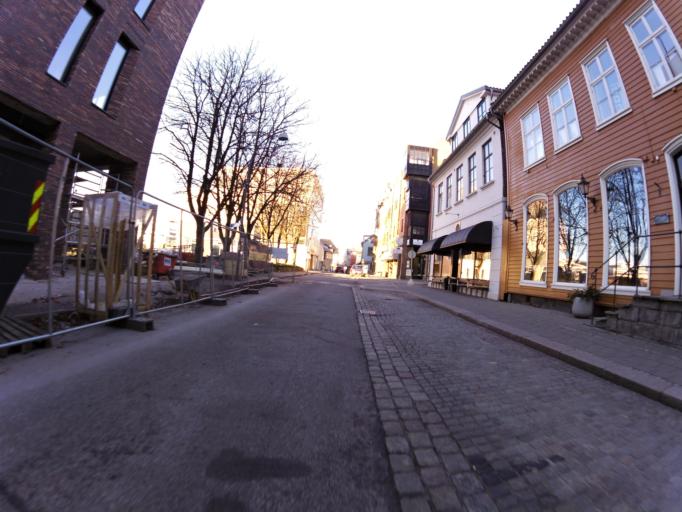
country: NO
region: Ostfold
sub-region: Fredrikstad
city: Fredrikstad
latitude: 59.2118
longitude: 10.9371
